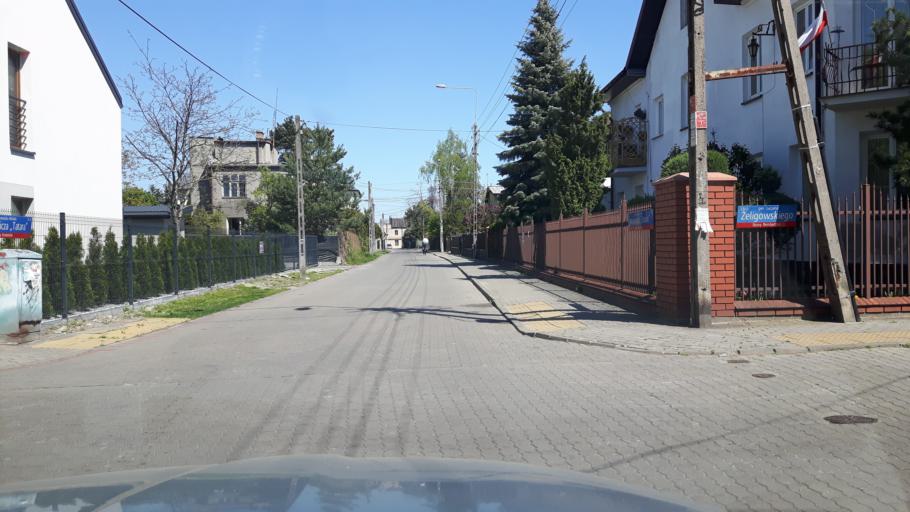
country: PL
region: Masovian Voivodeship
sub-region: Warszawa
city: Rembertow
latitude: 52.2540
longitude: 21.1602
